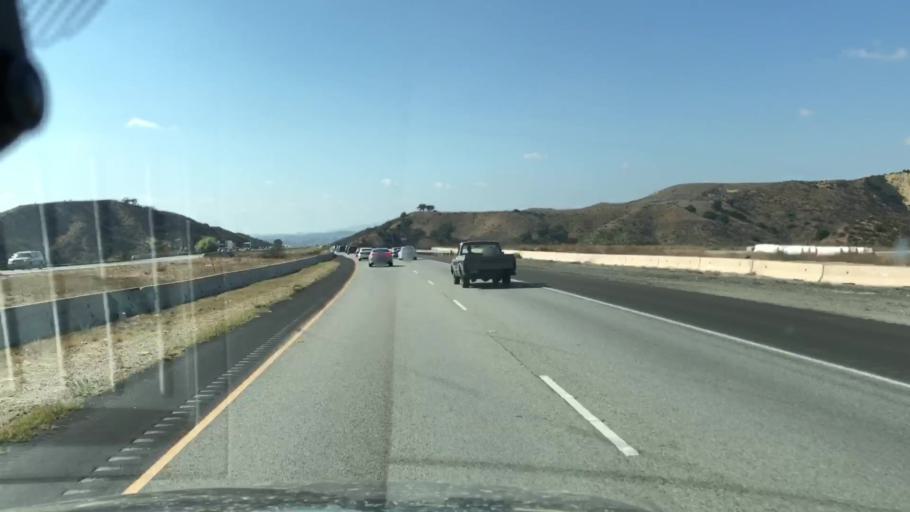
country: US
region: California
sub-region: Ventura County
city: Simi Valley
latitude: 34.2908
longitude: -118.8085
